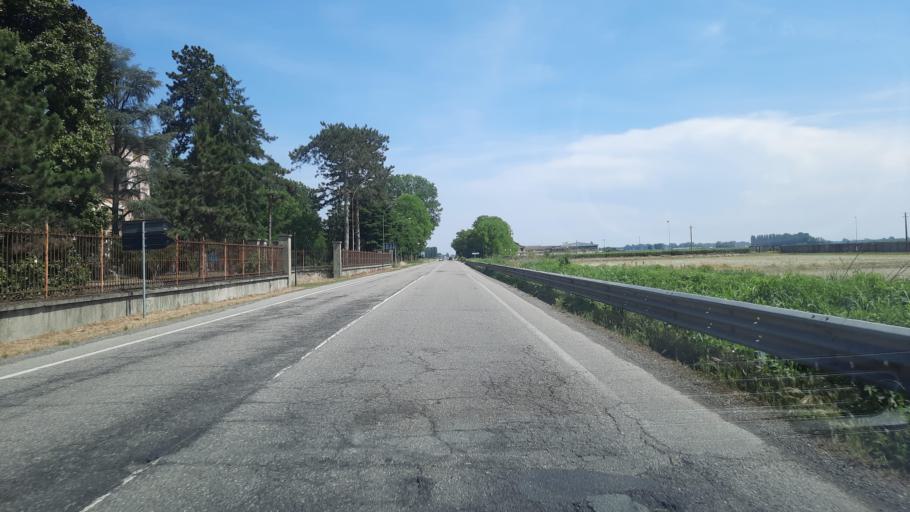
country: IT
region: Lombardy
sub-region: Provincia di Pavia
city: Mortara
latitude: 45.2494
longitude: 8.7557
